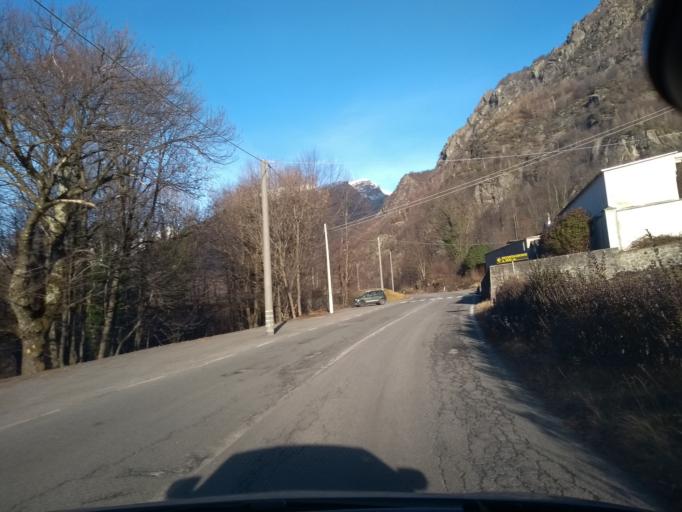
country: IT
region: Piedmont
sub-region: Provincia di Torino
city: Cantoira
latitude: 45.3474
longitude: 7.3721
